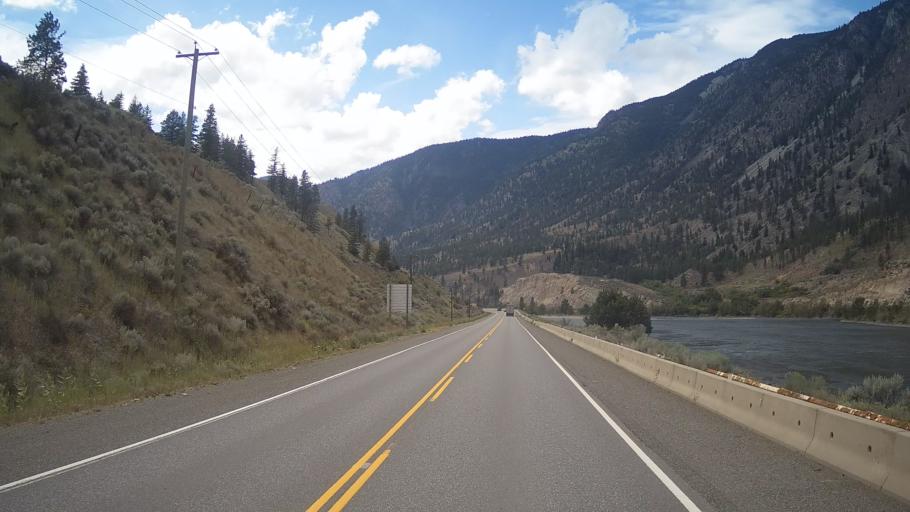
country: CA
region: British Columbia
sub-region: Thompson-Nicola Regional District
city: Ashcroft
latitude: 50.4082
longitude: -121.3675
